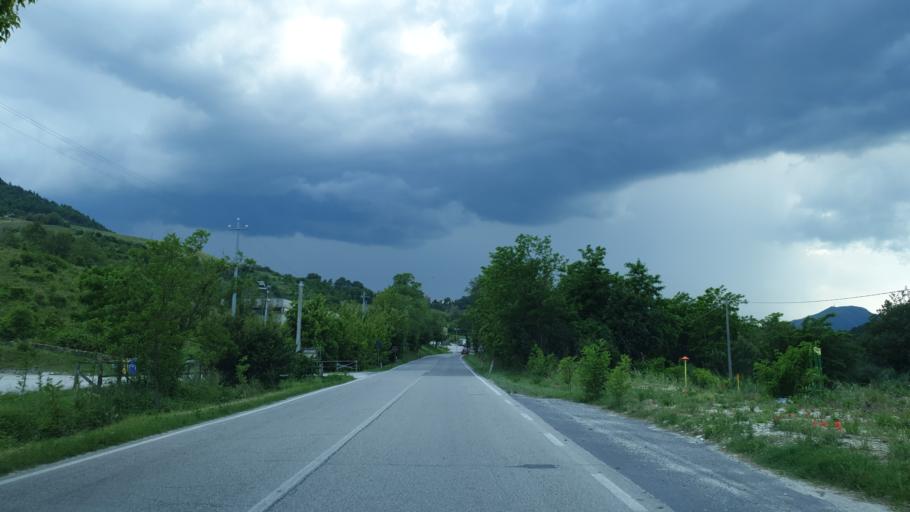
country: IT
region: Emilia-Romagna
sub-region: Provincia di Rimini
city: Pietracuta
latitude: 43.9409
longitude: 12.3545
